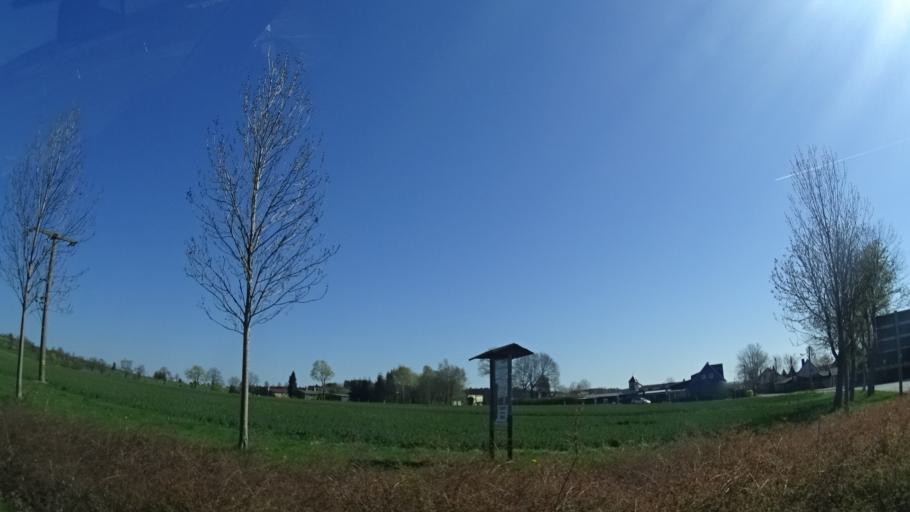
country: DE
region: Thuringia
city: Bohlen
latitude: 50.5908
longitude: 11.0409
